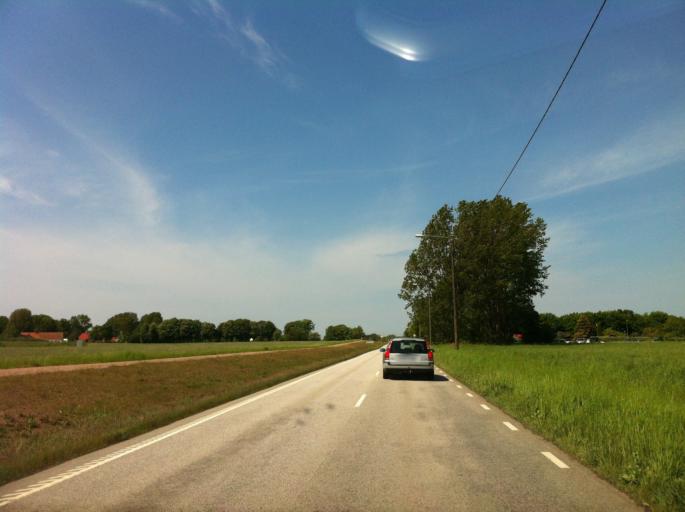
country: SE
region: Skane
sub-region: Helsingborg
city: Glumslov
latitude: 55.9246
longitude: 12.8438
